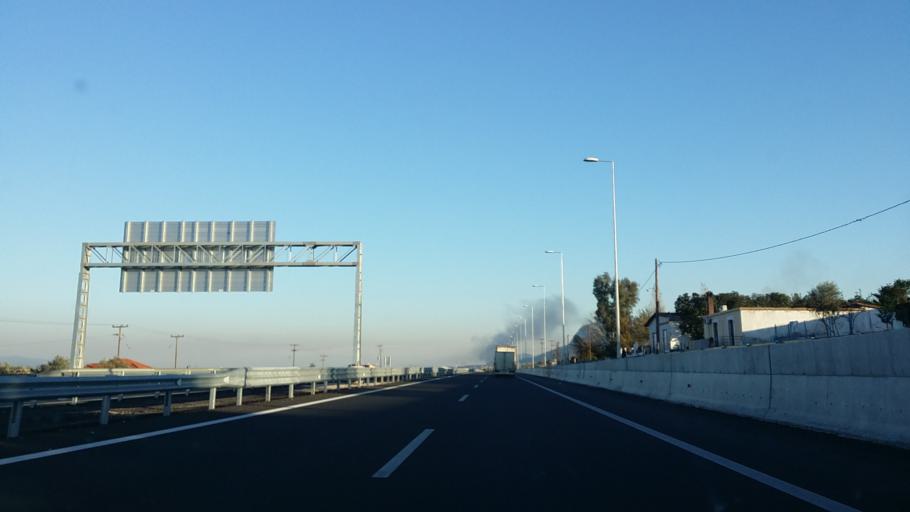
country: GR
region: Peloponnese
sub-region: Nomos Korinthias
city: Zevgolateio
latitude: 37.9252
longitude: 22.7990
